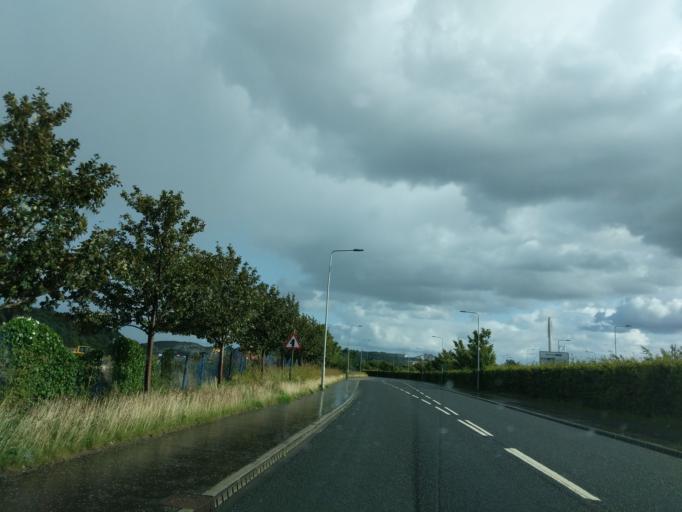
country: GB
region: Scotland
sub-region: Fife
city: Rosyth
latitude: 56.0229
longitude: -3.4267
